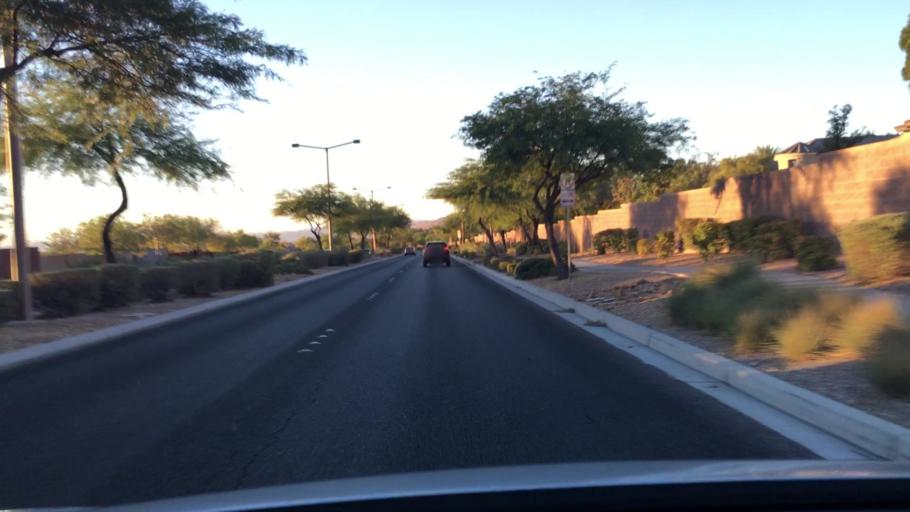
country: US
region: Nevada
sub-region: Clark County
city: Summerlin South
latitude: 36.1504
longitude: -115.3429
